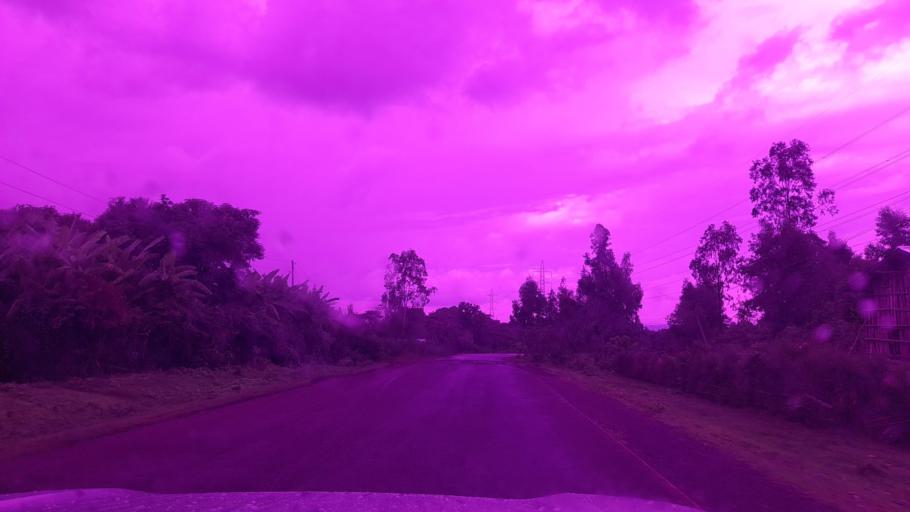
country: ET
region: Oromiya
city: Jima
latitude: 7.7085
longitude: 37.0606
